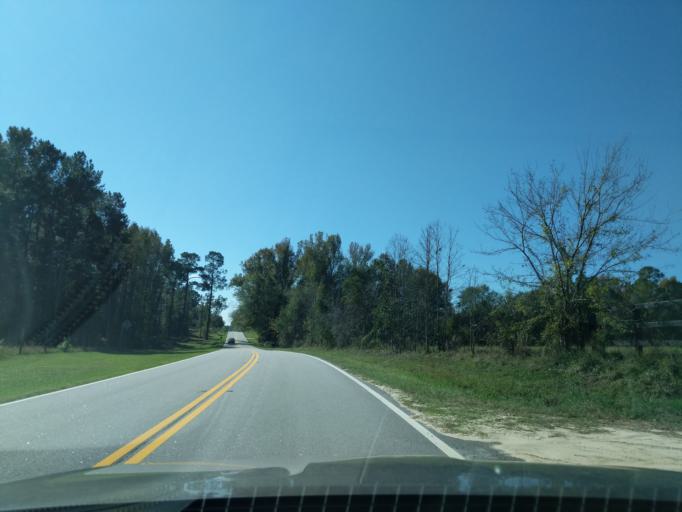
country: US
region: Georgia
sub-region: Richmond County
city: Hephzibah
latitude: 33.2986
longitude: -82.0213
